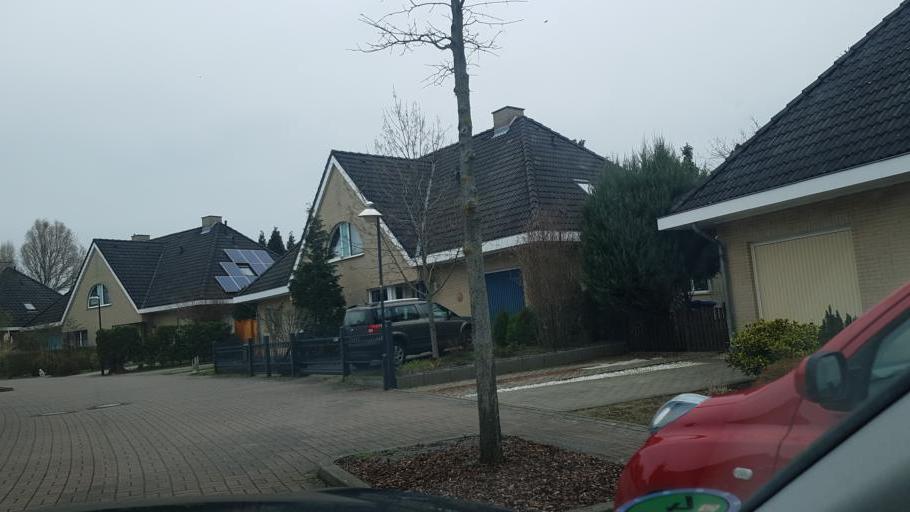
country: DE
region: Brandenburg
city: Mittenwalde
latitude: 52.2856
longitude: 13.5402
